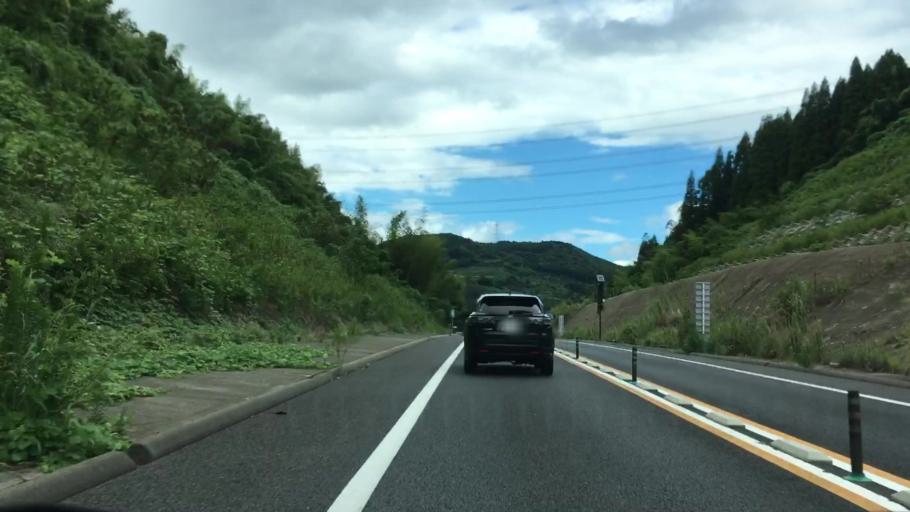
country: JP
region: Saga Prefecture
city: Karatsu
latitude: 33.3889
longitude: 129.9348
